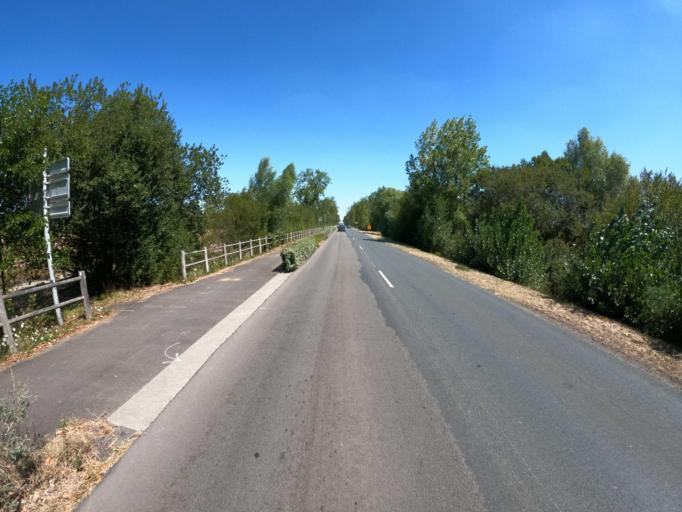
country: FR
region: Pays de la Loire
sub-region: Departement de la Vendee
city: Le Perrier
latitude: 46.8202
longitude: -1.9872
